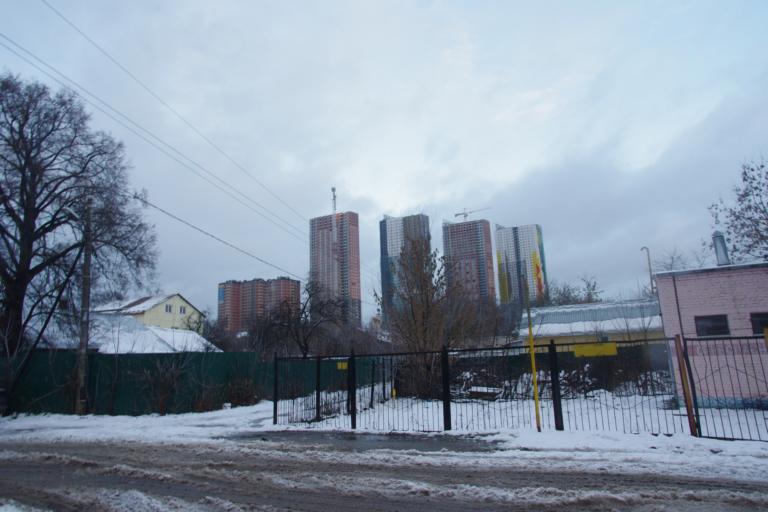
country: RU
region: Moskovskaya
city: Pavshino
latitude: 55.8112
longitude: 37.3532
